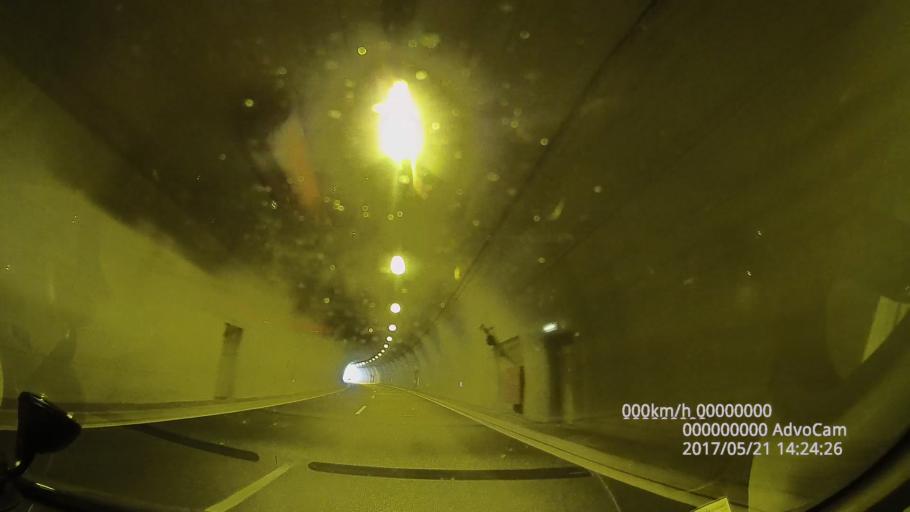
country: GR
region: Central Greece
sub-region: Nomos Fthiotidos
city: Ayios Konstandinos
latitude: 38.7460
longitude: 22.8731
